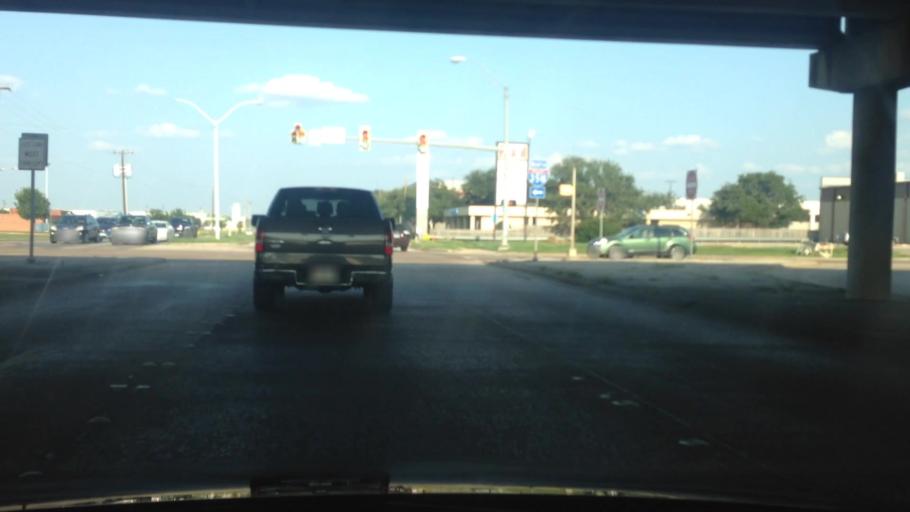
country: US
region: Texas
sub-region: Tarrant County
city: Everman
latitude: 32.6275
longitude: -97.3216
